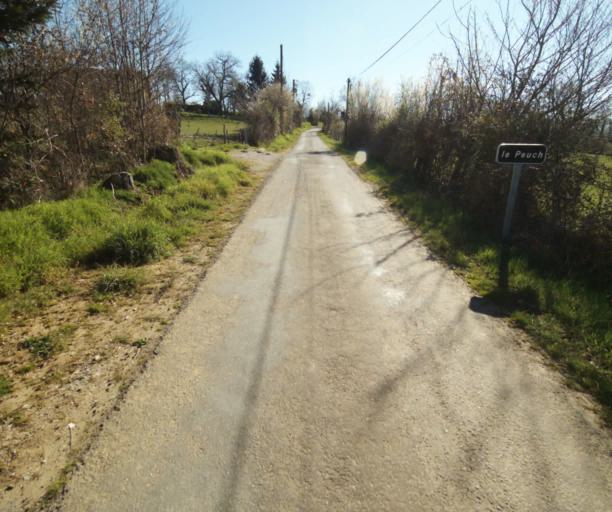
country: FR
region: Limousin
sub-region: Departement de la Correze
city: Chamboulive
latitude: 45.4060
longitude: 1.7028
